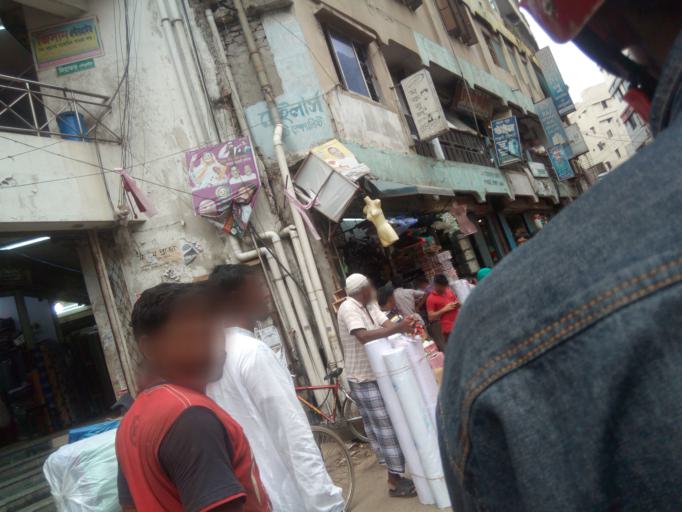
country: BD
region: Dhaka
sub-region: Dhaka
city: Dhaka
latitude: 23.7074
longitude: 90.4095
